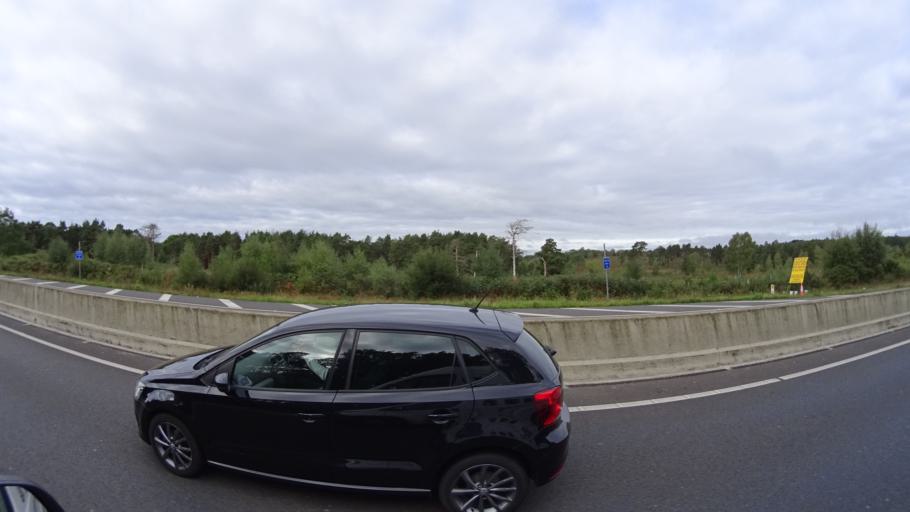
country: GB
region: England
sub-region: Hampshire
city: Ringwood
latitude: 50.8325
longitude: -1.8103
